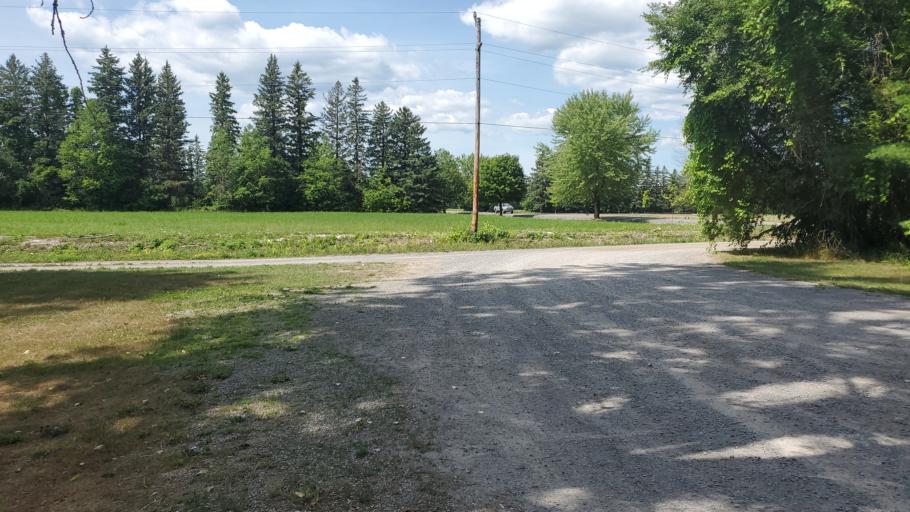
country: CA
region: Ontario
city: Prescott
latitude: 45.0299
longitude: -75.6459
